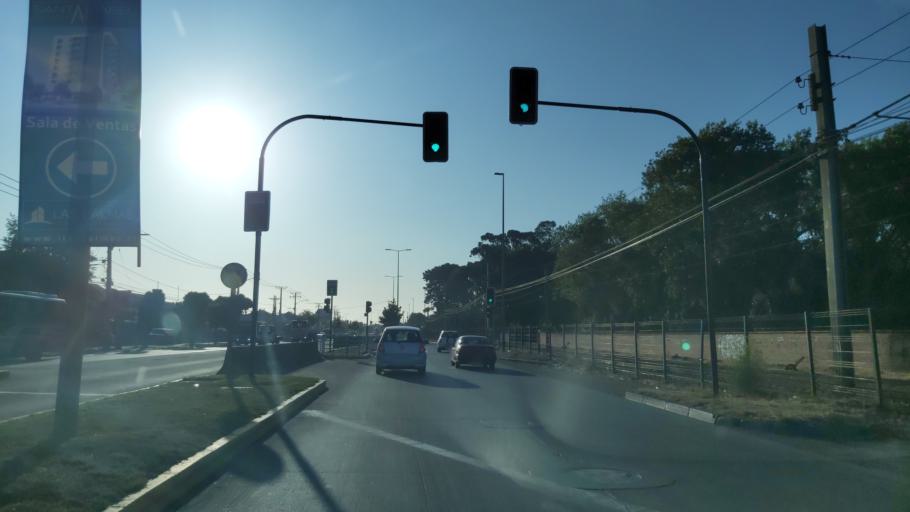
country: CL
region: Biobio
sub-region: Provincia de Concepcion
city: Concepcion
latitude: -36.8388
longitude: -73.0925
